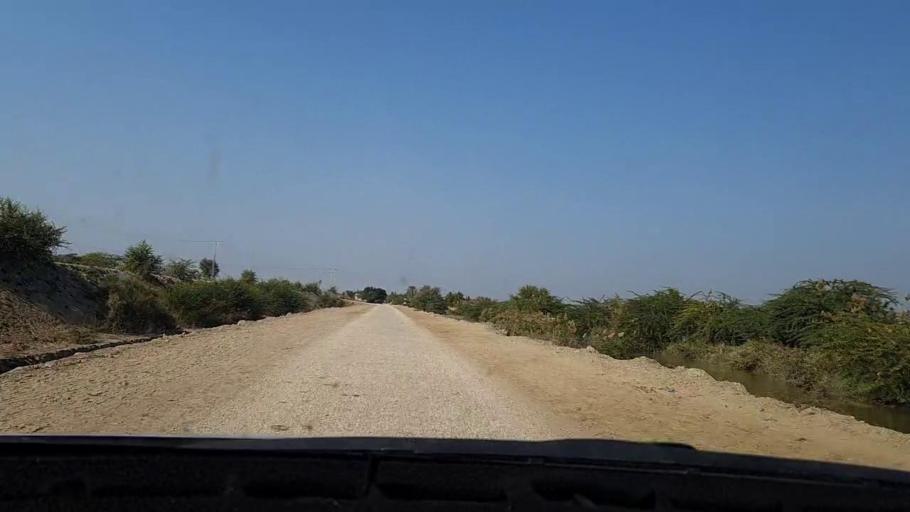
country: PK
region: Sindh
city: Tando Mittha Khan
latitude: 25.8271
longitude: 69.2898
